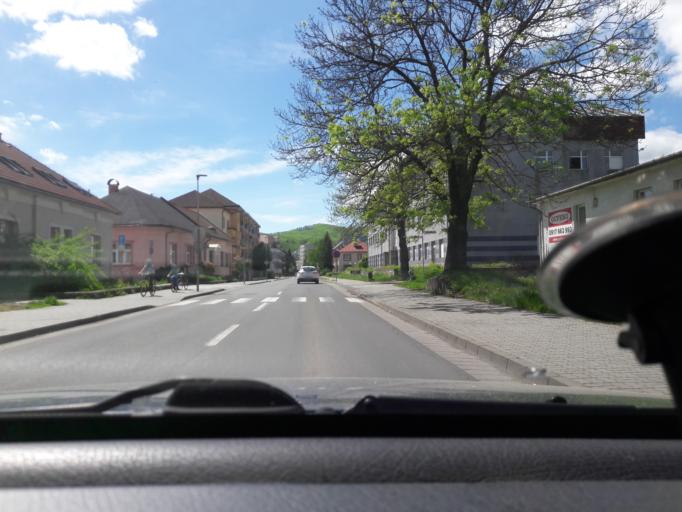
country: SK
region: Banskobystricky
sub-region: Okres Banska Bystrica
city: Zvolen
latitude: 48.5801
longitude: 19.1229
